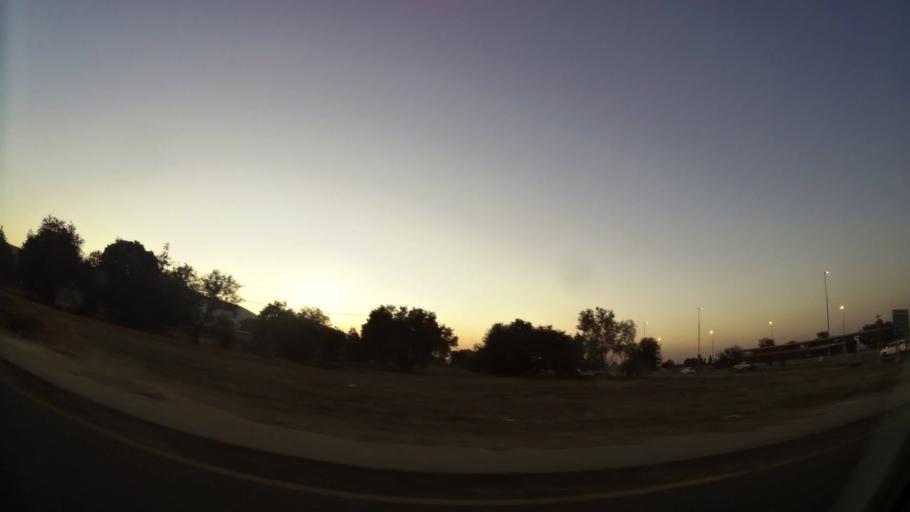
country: ZA
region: North-West
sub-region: Bojanala Platinum District Municipality
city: Rustenburg
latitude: -25.6546
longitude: 27.2199
